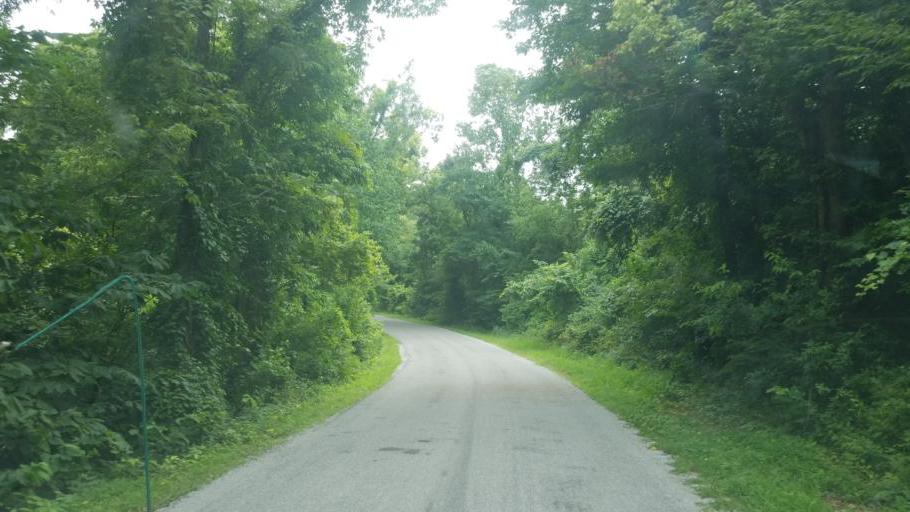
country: US
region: Illinois
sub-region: Jackson County
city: Murphysboro
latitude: 37.6788
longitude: -89.3923
